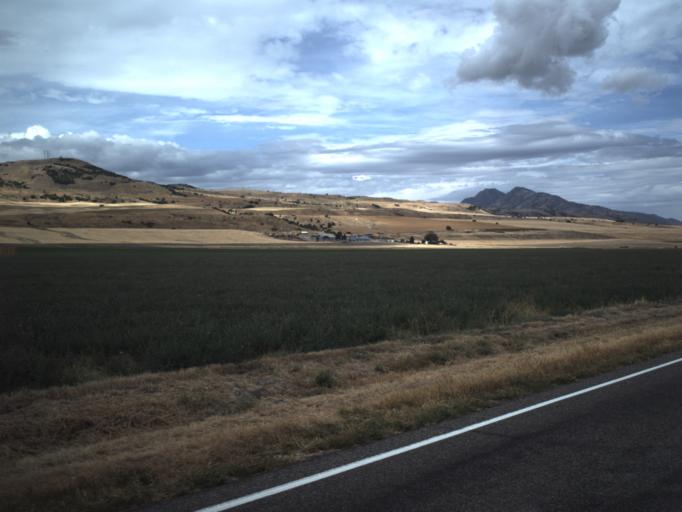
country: US
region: Utah
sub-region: Cache County
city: Benson
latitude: 41.8162
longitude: -111.9969
